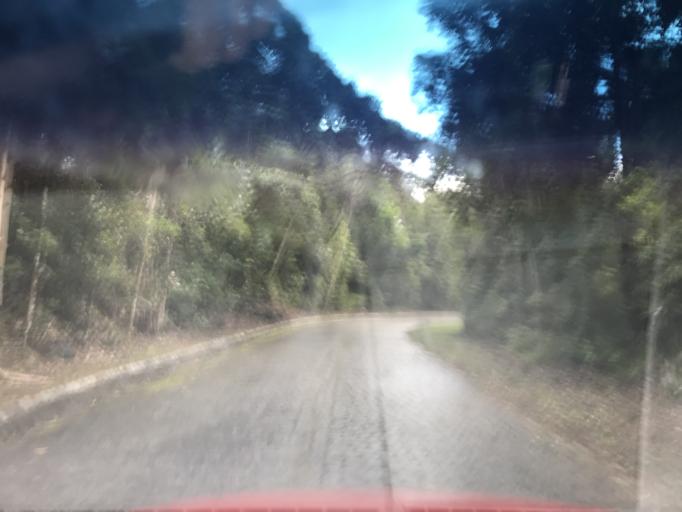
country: BR
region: Bahia
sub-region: Gandu
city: Gandu
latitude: -13.9039
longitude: -39.4613
